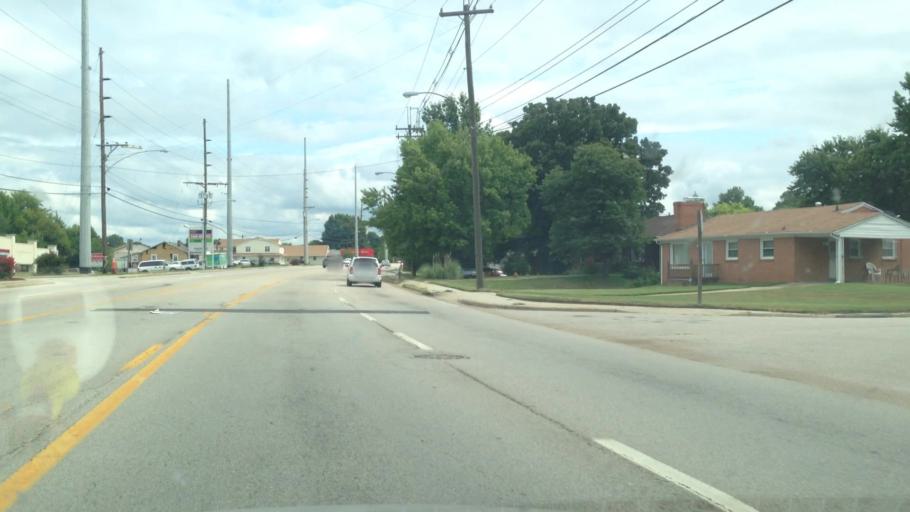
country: US
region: Virginia
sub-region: City of Danville
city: Danville
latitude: 36.6245
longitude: -79.4033
